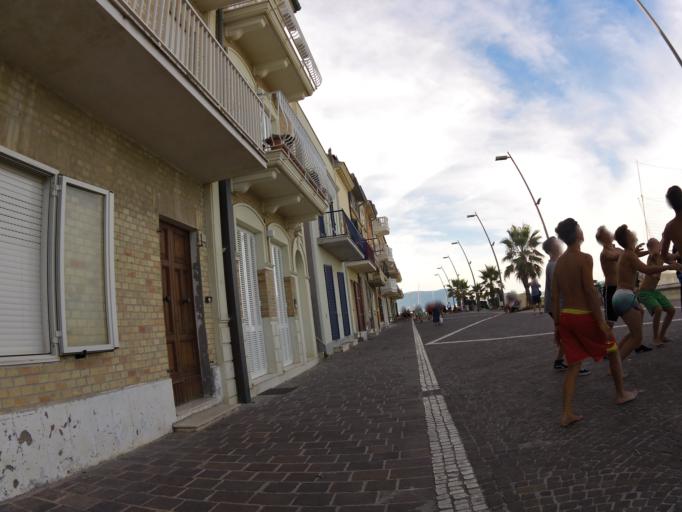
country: IT
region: The Marches
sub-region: Provincia di Macerata
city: Porto Recanati
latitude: 43.4377
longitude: 13.6626
